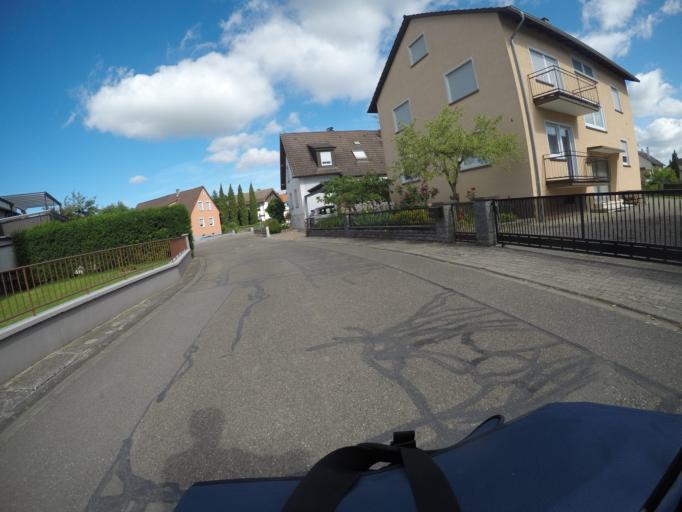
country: DE
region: Baden-Wuerttemberg
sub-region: Karlsruhe Region
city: Au am Rhein
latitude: 48.9357
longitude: 8.2071
